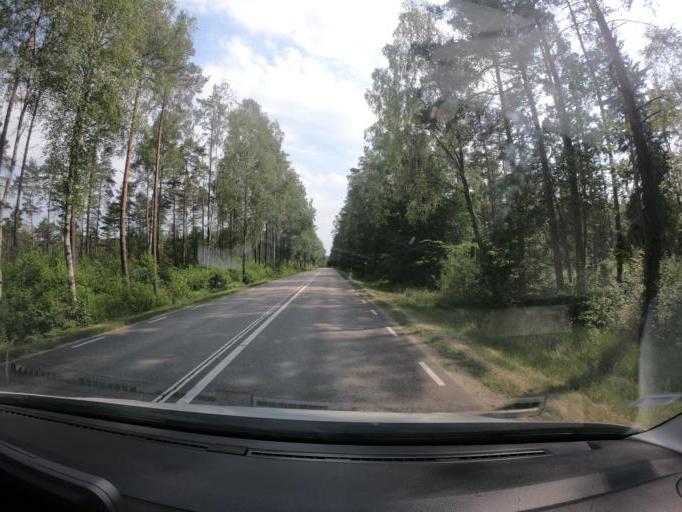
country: SE
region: Skane
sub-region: Hassleholms Kommun
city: Bjarnum
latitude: 56.3571
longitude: 13.6597
